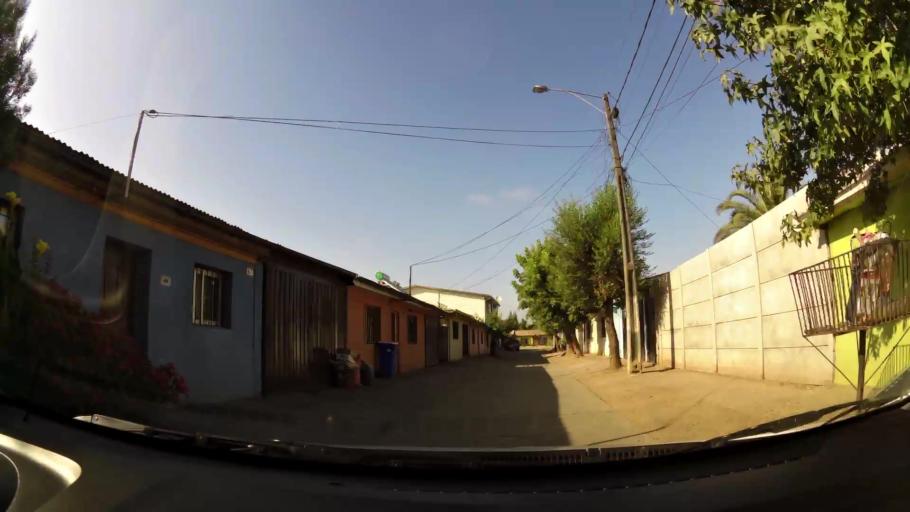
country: CL
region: Maule
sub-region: Provincia de Talca
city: Talca
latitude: -35.4073
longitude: -71.6621
